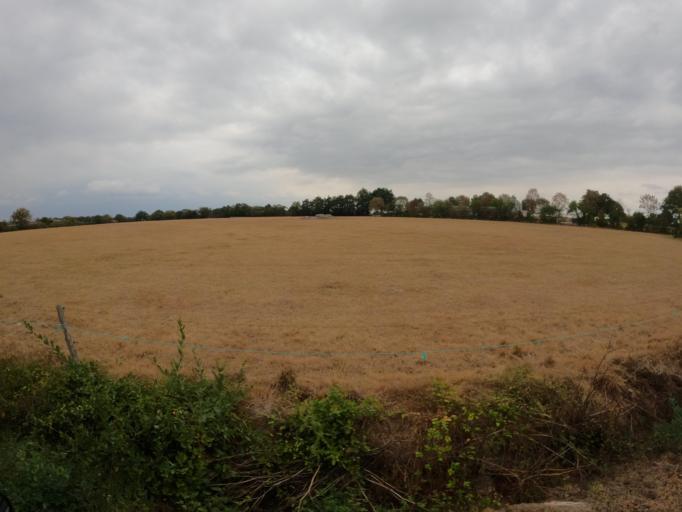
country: FR
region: Pays de la Loire
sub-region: Departement de la Vendee
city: La Boissiere-de-Montaigu
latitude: 46.9763
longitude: -1.1873
